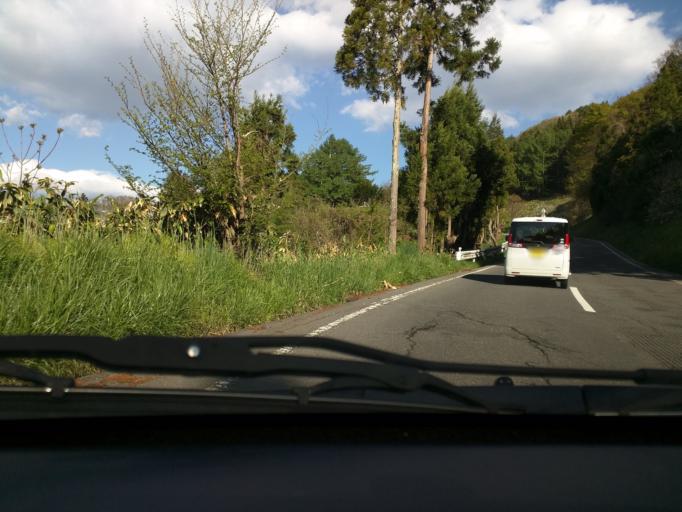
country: JP
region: Nagano
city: Nagano-shi
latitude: 36.6804
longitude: 138.1718
